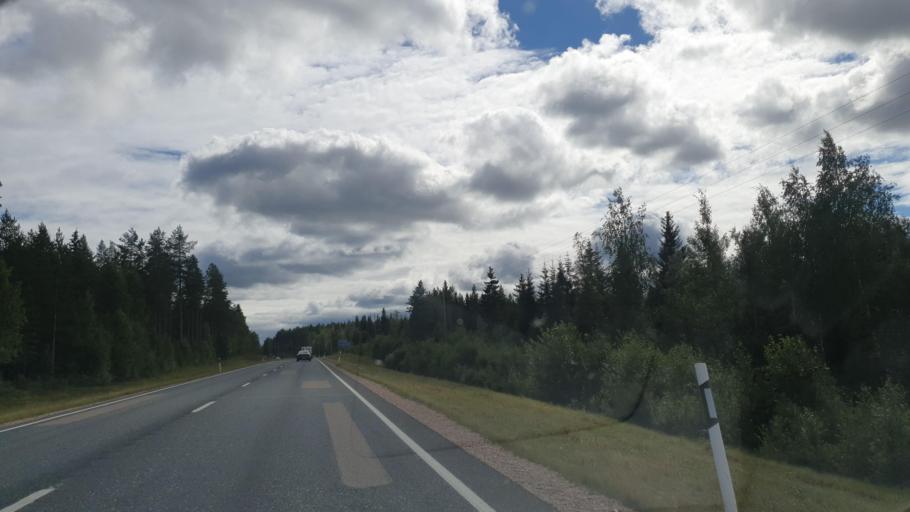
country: FI
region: Kainuu
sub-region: Kajaani
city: Kajaani
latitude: 64.1001
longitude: 27.4494
